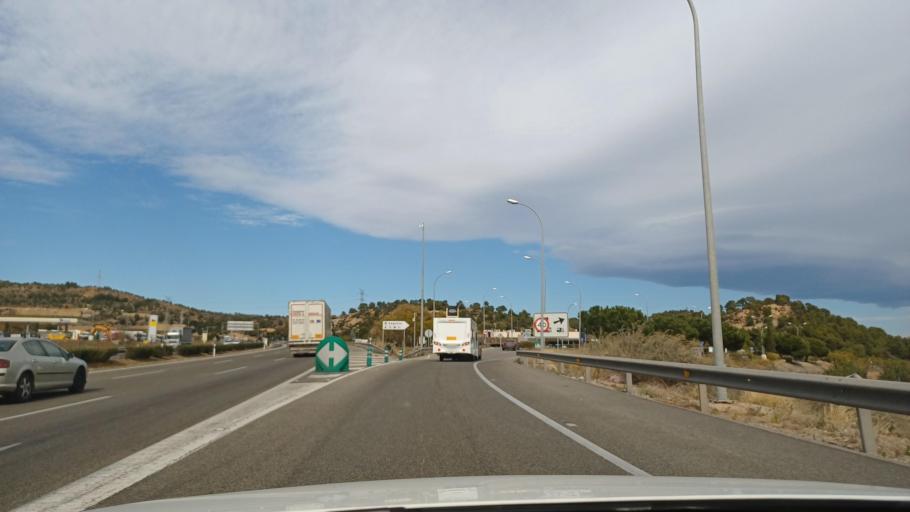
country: ES
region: Valencia
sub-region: Provincia de Valencia
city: Pucol
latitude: 39.6479
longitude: -0.3004
